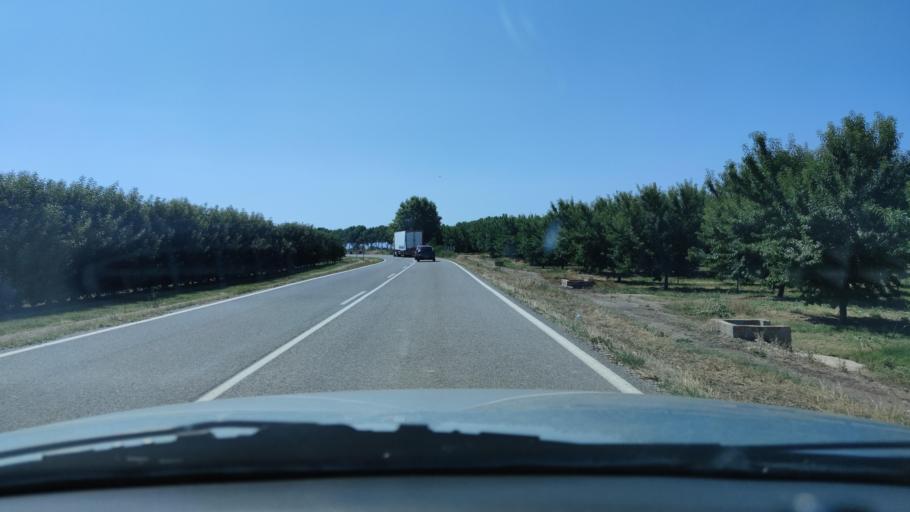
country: ES
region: Catalonia
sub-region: Provincia de Lleida
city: Ivars d'Urgell
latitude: 41.6948
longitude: 0.9862
